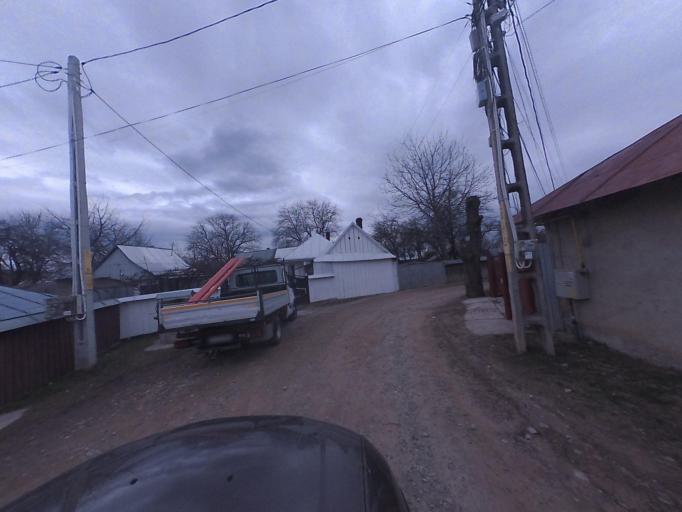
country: RO
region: Neamt
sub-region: Oras Targu Neamt
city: Humulesti
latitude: 47.1960
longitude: 26.3403
